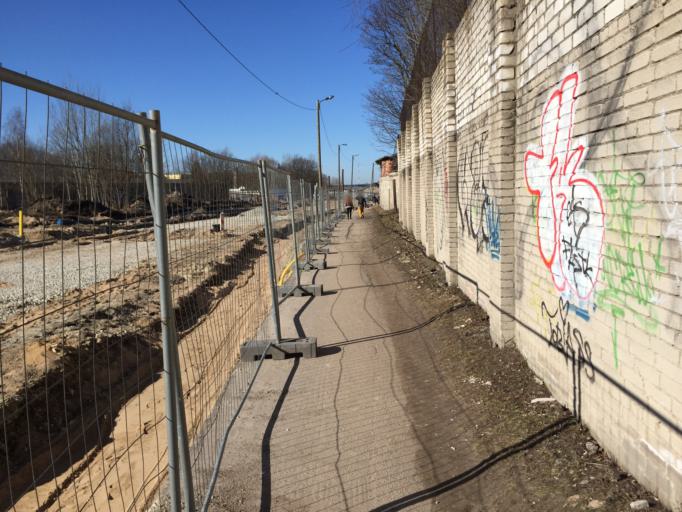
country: EE
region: Harju
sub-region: Tallinna linn
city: Tallinn
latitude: 59.4493
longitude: 24.7418
